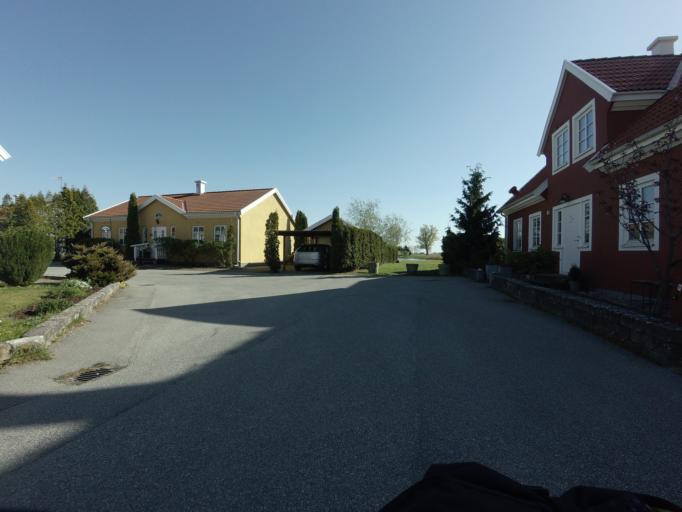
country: SE
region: Skane
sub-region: Landskrona
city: Asmundtorp
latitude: 55.8541
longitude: 12.9065
